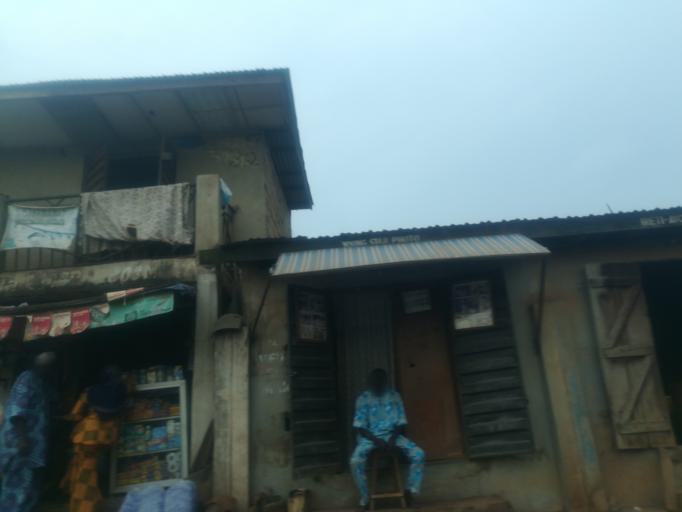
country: NG
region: Oyo
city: Ibadan
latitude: 7.4365
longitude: 3.9212
